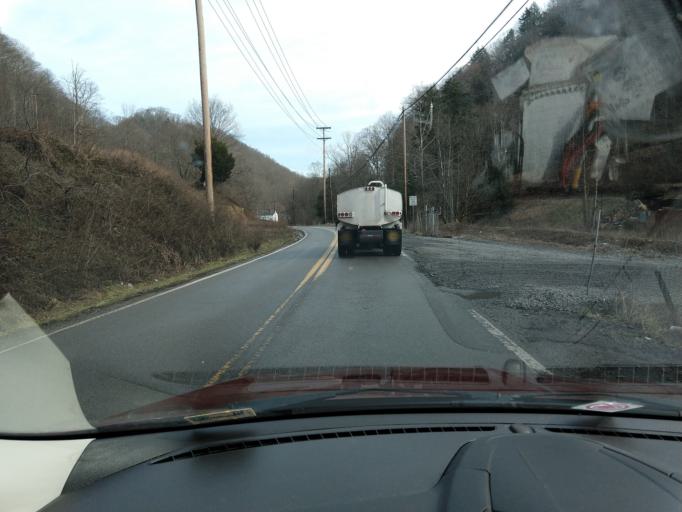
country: US
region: West Virginia
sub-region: McDowell County
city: Welch
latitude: 37.3338
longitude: -81.6793
